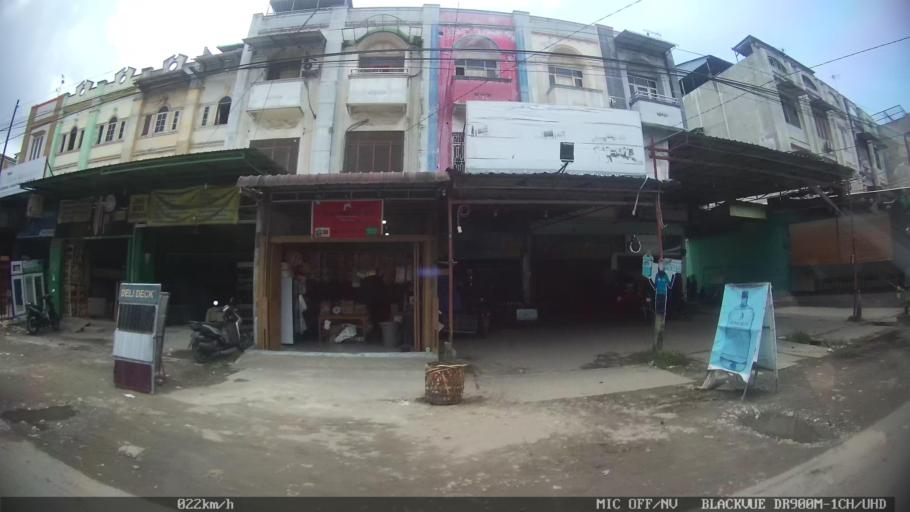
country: ID
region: North Sumatra
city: Labuhan Deli
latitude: 3.7042
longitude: 98.6587
